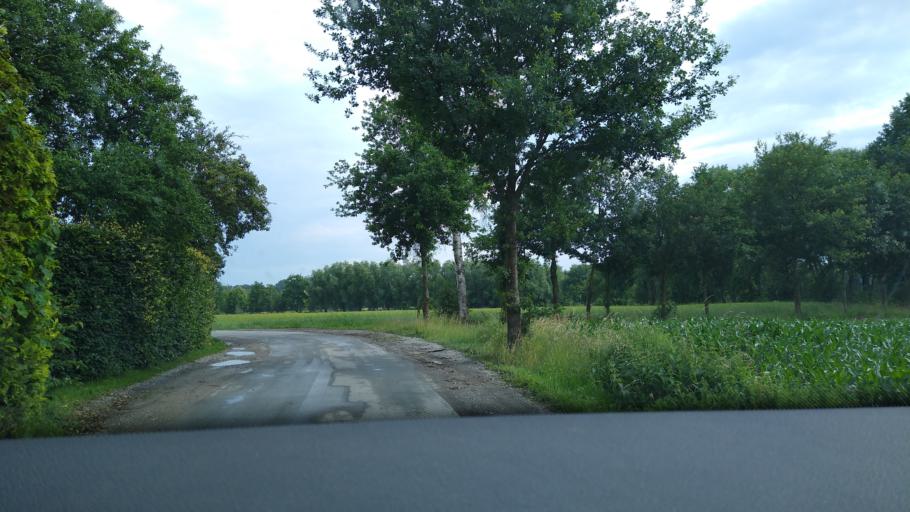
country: DE
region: North Rhine-Westphalia
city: Rietberg
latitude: 51.8422
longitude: 8.4367
